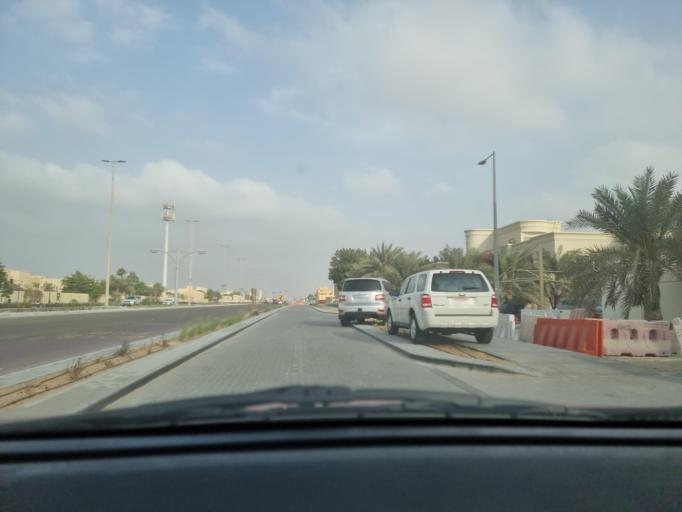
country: AE
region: Abu Dhabi
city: Abu Dhabi
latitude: 24.4258
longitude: 54.5503
